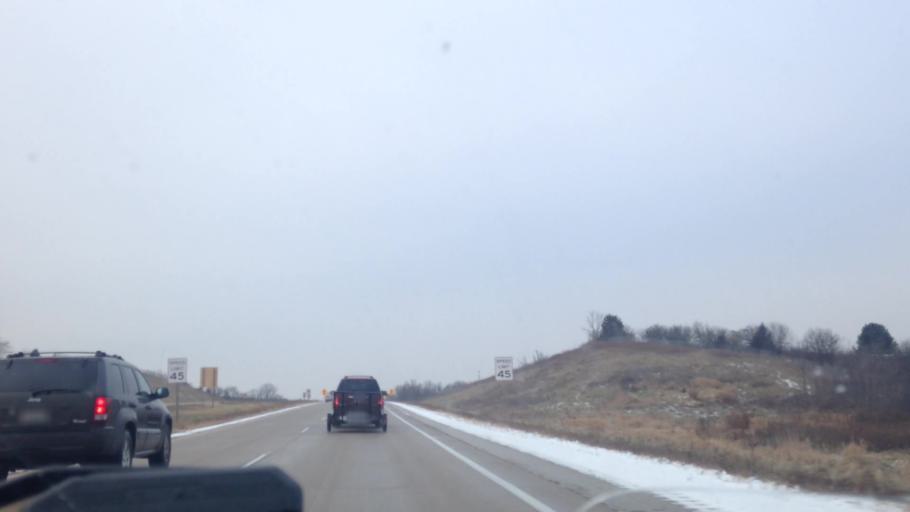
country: US
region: Wisconsin
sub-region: Waukesha County
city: Oconomowoc
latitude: 43.1268
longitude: -88.4800
